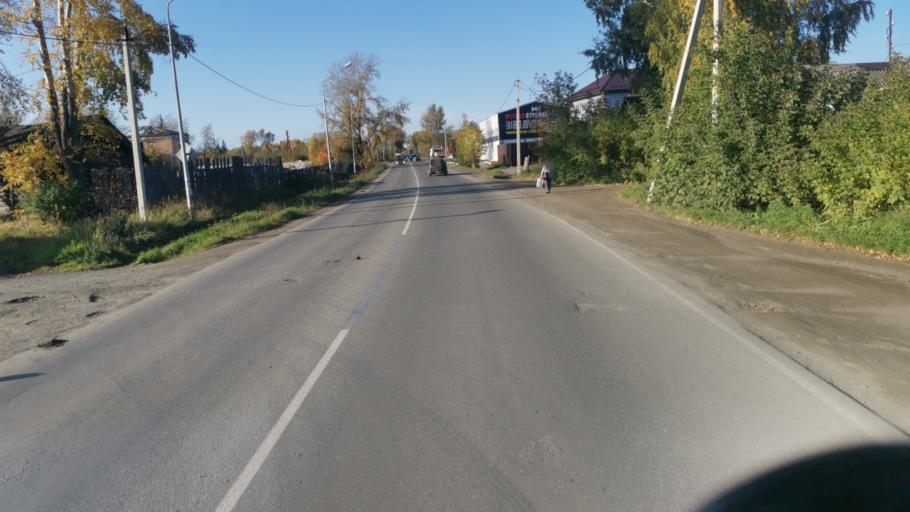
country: RU
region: Sverdlovsk
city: Nizhniy Tagil
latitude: 57.9307
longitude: 59.9353
